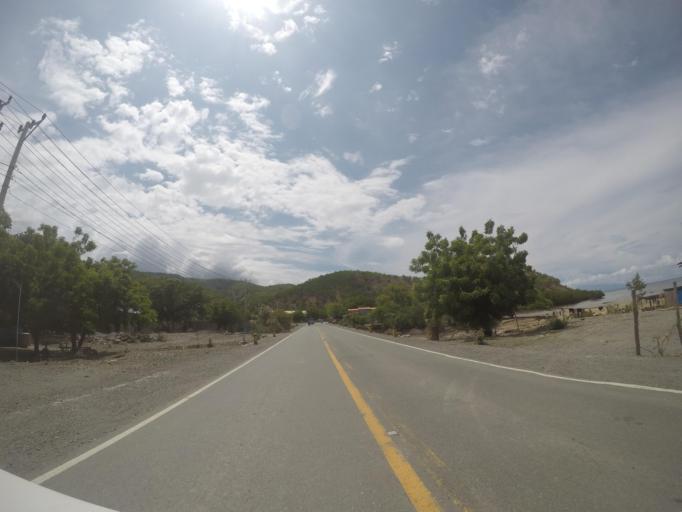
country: TL
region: Liquica
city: Liquica
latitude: -8.5721
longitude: 125.4475
